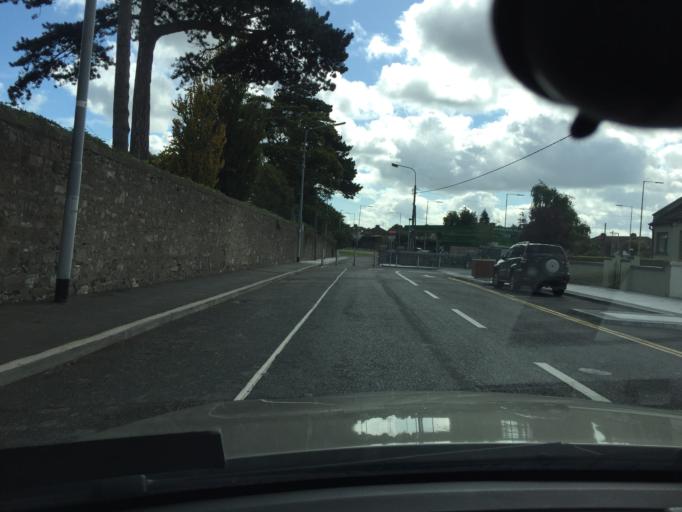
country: IE
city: Palmerstown
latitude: 53.3548
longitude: -6.3679
